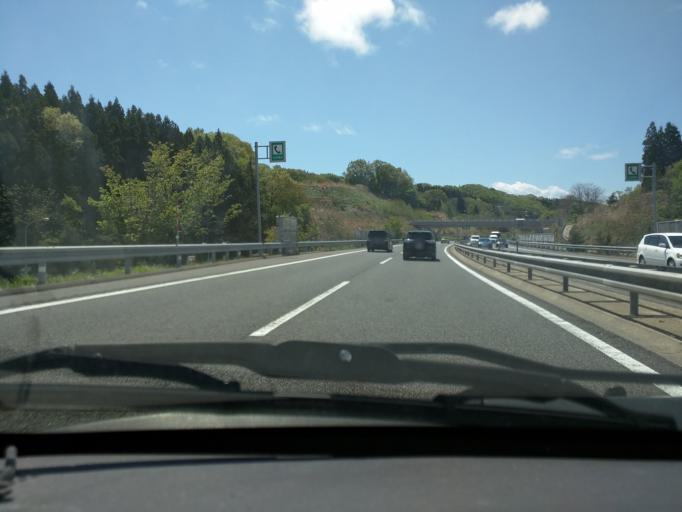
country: JP
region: Nagano
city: Nakano
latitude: 36.7971
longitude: 138.3212
